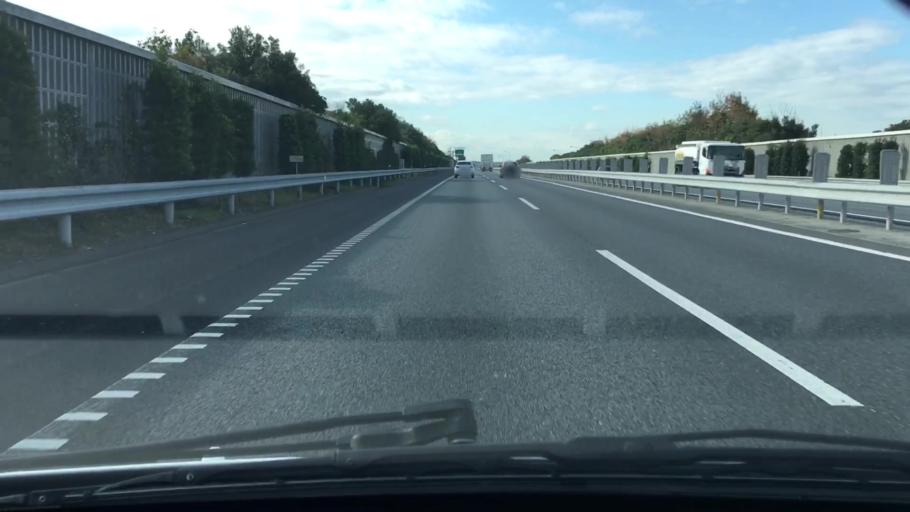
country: JP
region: Chiba
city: Ichihara
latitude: 35.5015
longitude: 140.0996
